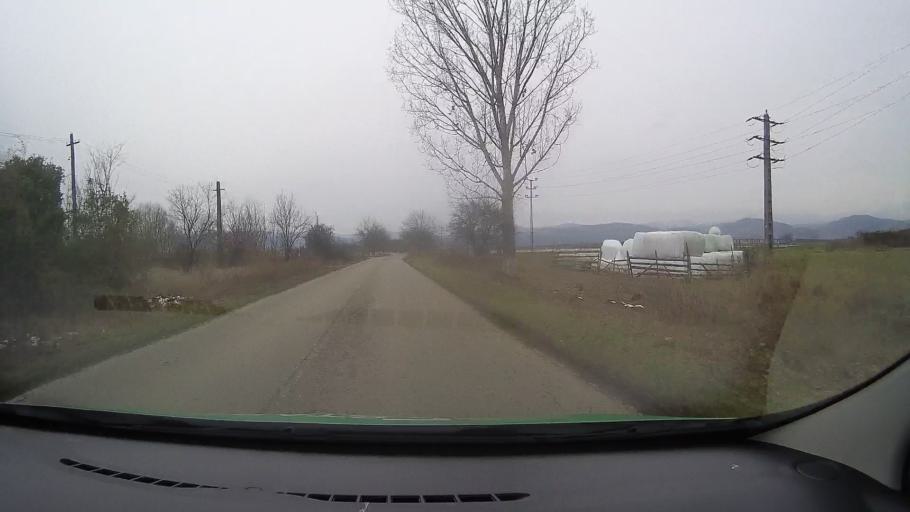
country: RO
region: Hunedoara
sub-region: Comuna Romos
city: Romos
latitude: 45.8798
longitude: 23.2580
